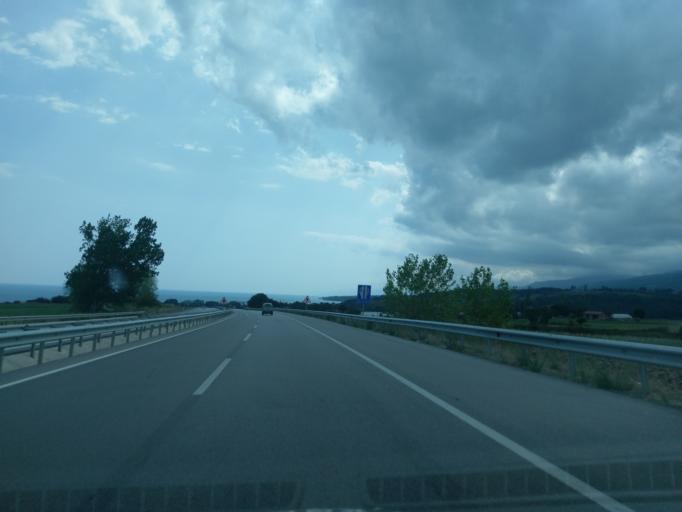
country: TR
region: Sinop
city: Gerze
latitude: 41.8434
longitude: 35.1403
